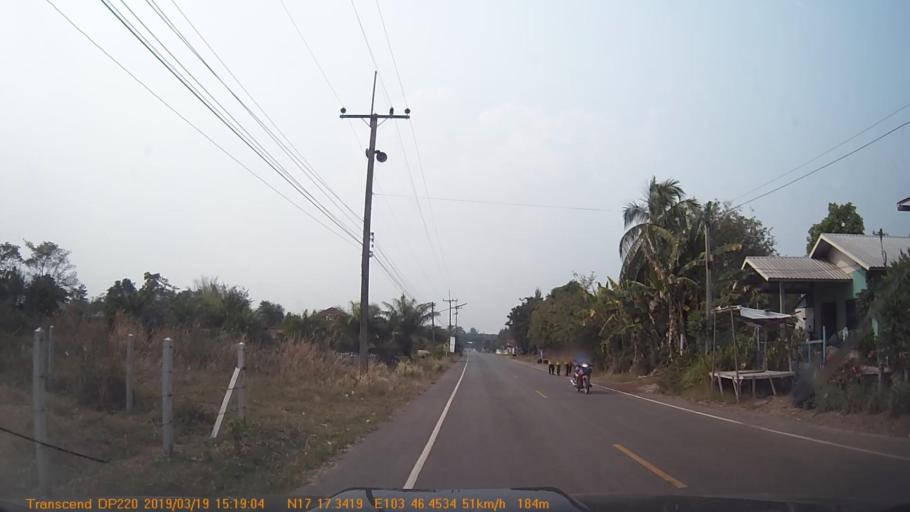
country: TH
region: Sakon Nakhon
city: Phanna Nikhom
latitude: 17.2892
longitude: 103.7741
